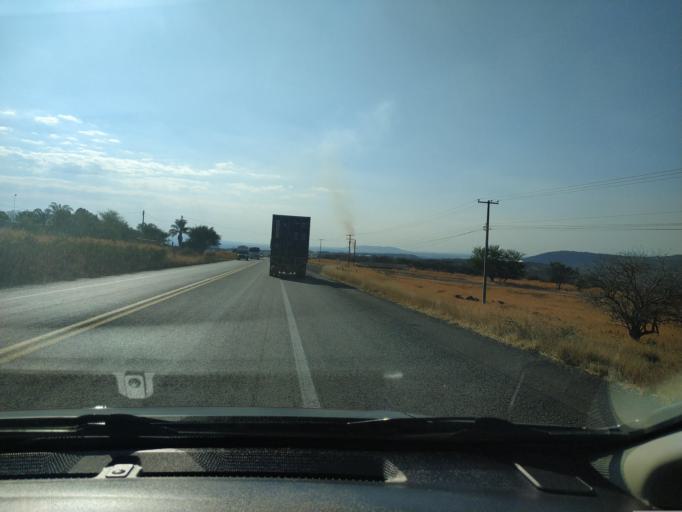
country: MX
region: Michoacan
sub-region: Yurecuaro
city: Yurecuaro
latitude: 20.3400
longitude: -102.2122
